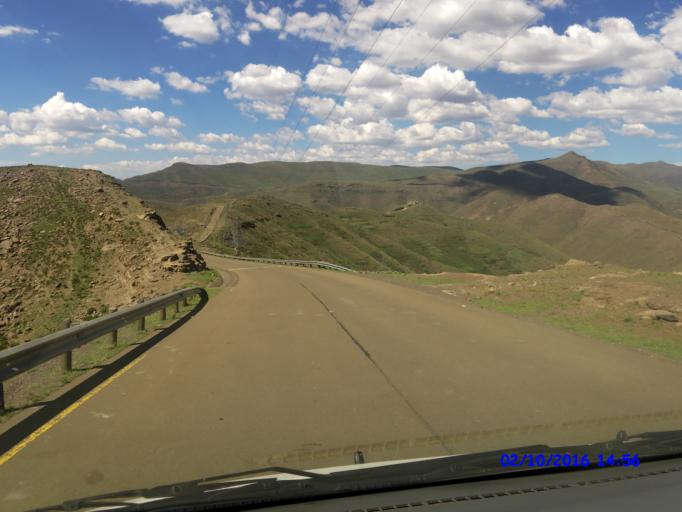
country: LS
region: Maseru
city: Nako
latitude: -29.4688
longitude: 28.0904
